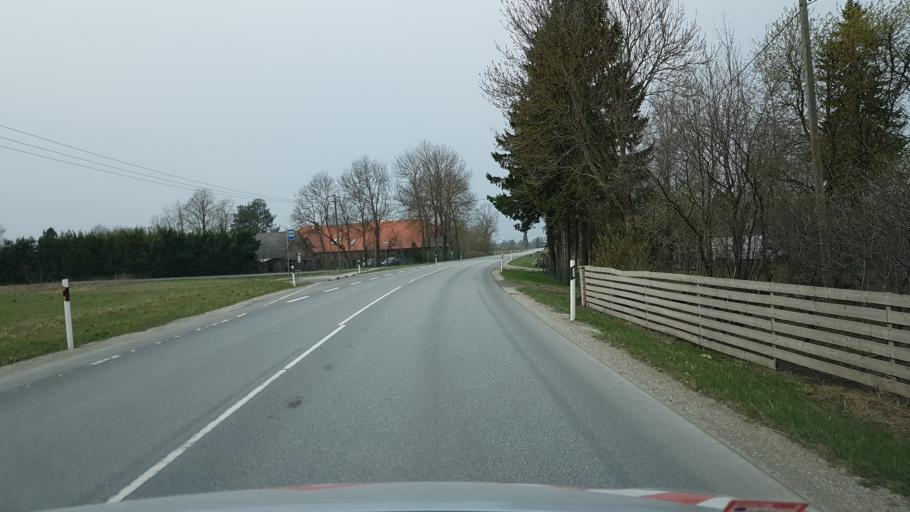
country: EE
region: Harju
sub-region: Joelaehtme vald
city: Loo
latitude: 59.3942
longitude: 24.9672
